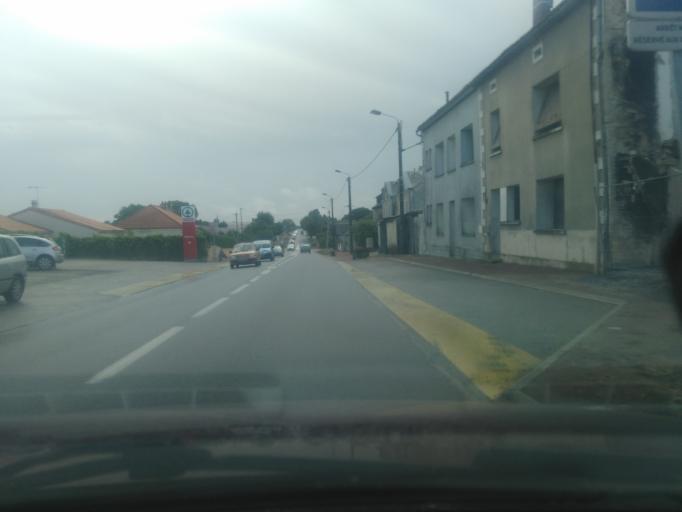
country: FR
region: Poitou-Charentes
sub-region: Departement des Deux-Sevres
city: Thenezay
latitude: 46.6614
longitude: -0.0025
